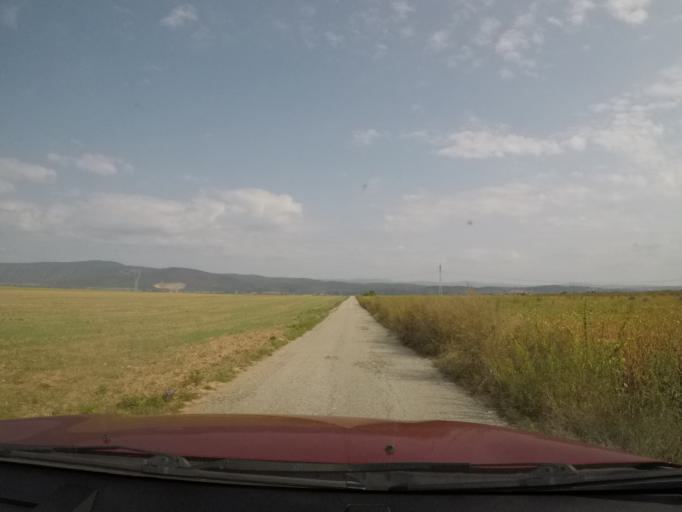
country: SK
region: Kosicky
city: Moldava nad Bodvou
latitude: 48.5831
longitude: 20.9566
